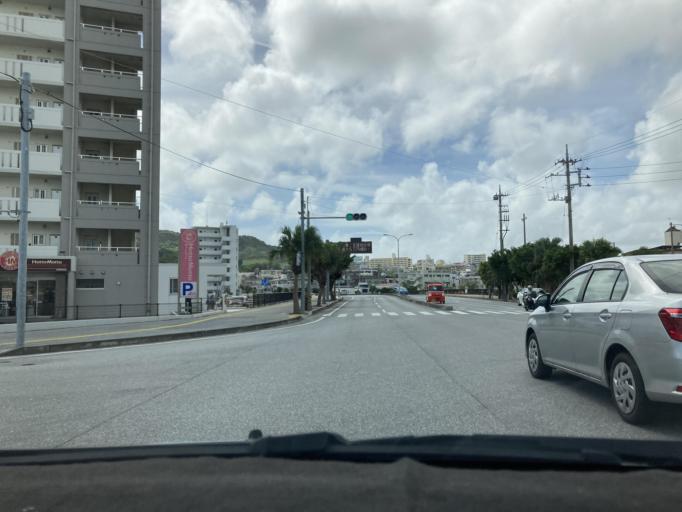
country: JP
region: Okinawa
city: Ginowan
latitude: 26.2038
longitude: 127.7612
